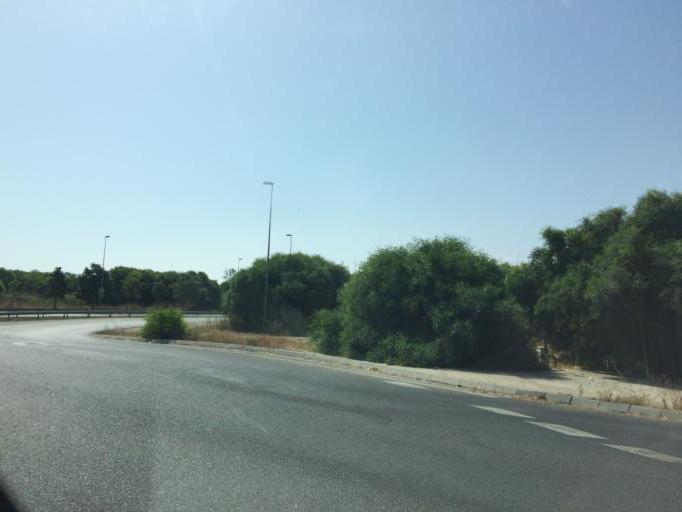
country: ES
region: Andalusia
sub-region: Provincia de Malaga
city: Torremolinos
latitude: 36.6567
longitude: -4.4846
